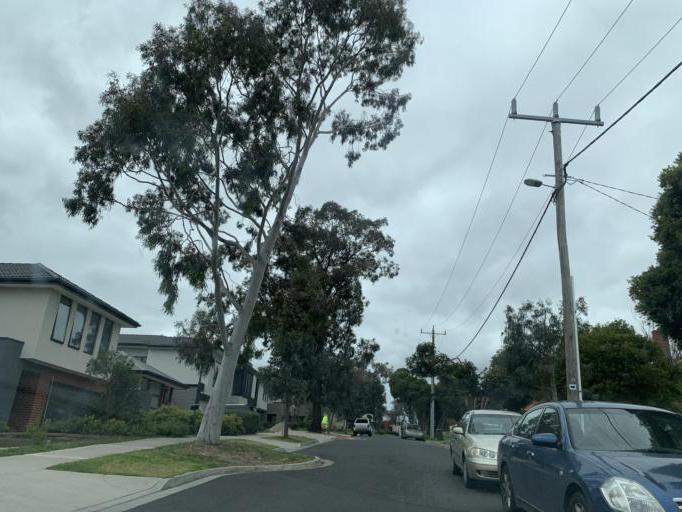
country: AU
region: Victoria
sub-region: Moreland
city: Coburg North
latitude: -37.7301
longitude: 144.9789
